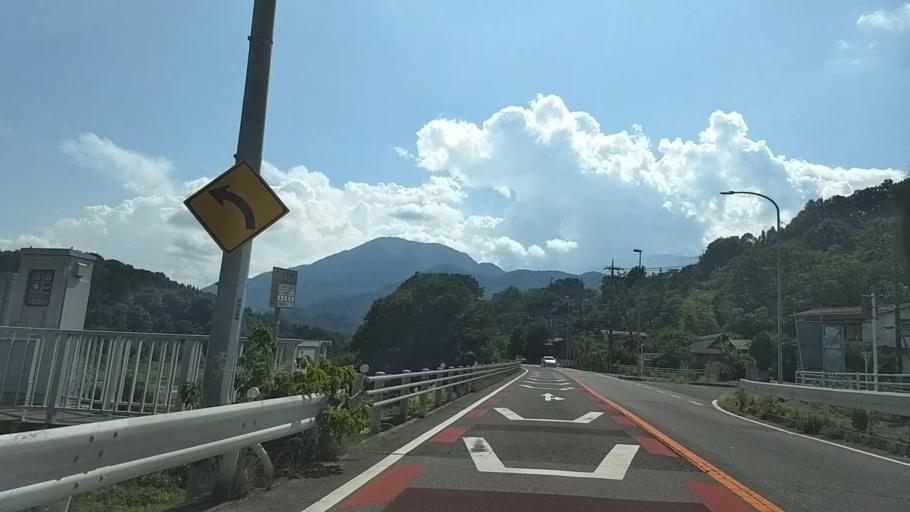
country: JP
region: Yamanashi
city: Ryuo
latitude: 35.4471
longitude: 138.4421
